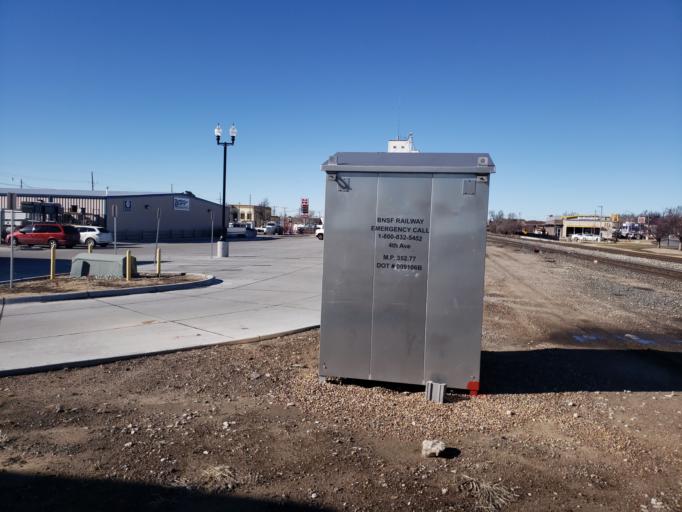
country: US
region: Kansas
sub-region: Ford County
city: Dodge City
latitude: 37.7524
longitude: -100.0216
